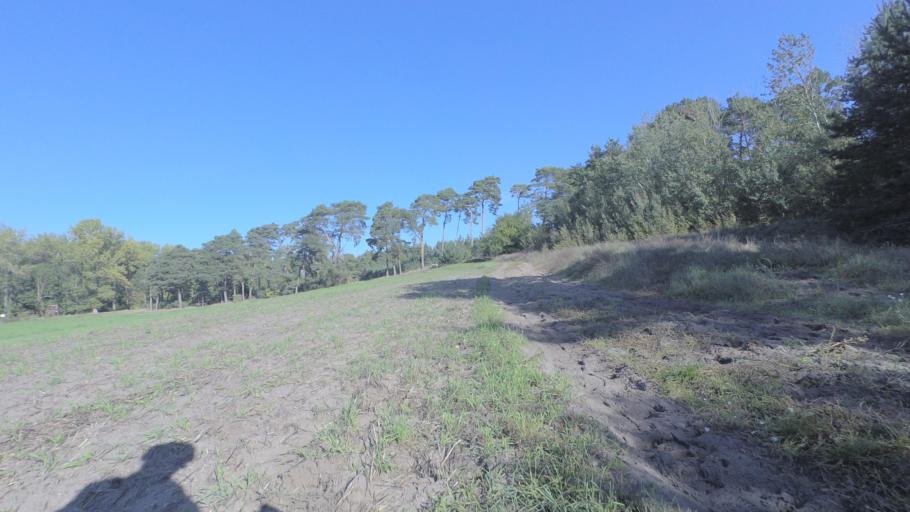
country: DE
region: Brandenburg
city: Rangsdorf
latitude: 52.2929
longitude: 13.3697
